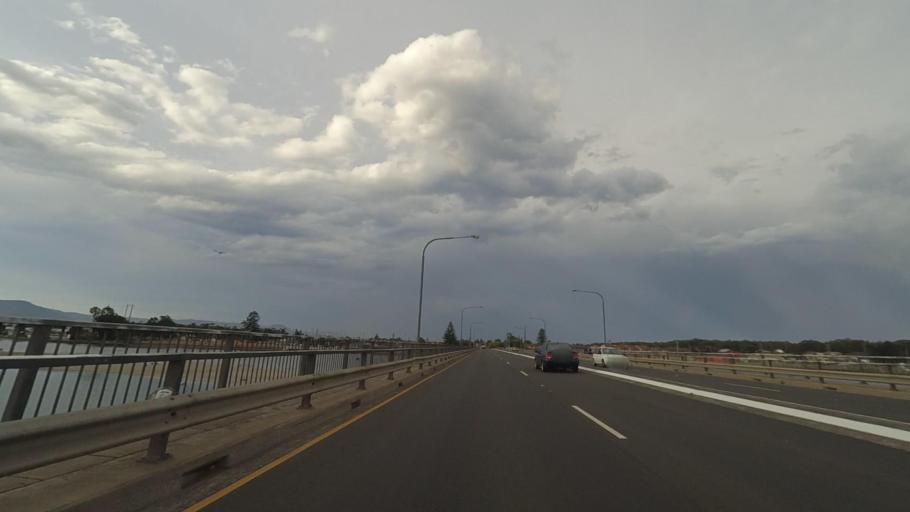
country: AU
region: New South Wales
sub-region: Shellharbour
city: Lake Illawarra
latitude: -34.5366
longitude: 150.8667
